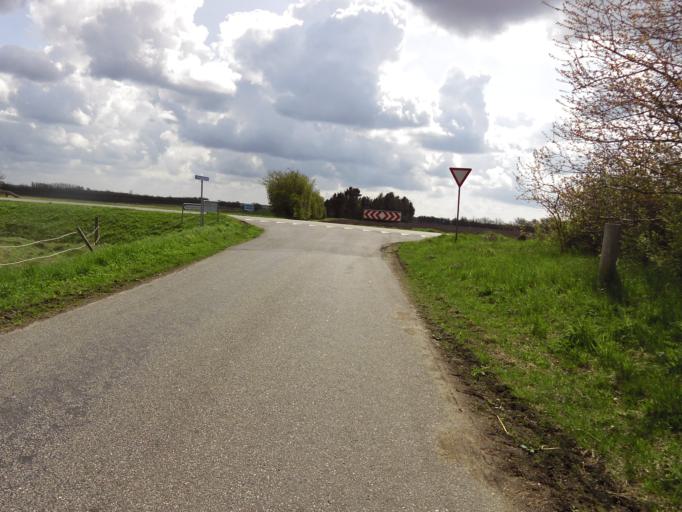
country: DK
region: South Denmark
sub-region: Tonder Kommune
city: Toftlund
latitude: 55.2031
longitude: 9.1643
